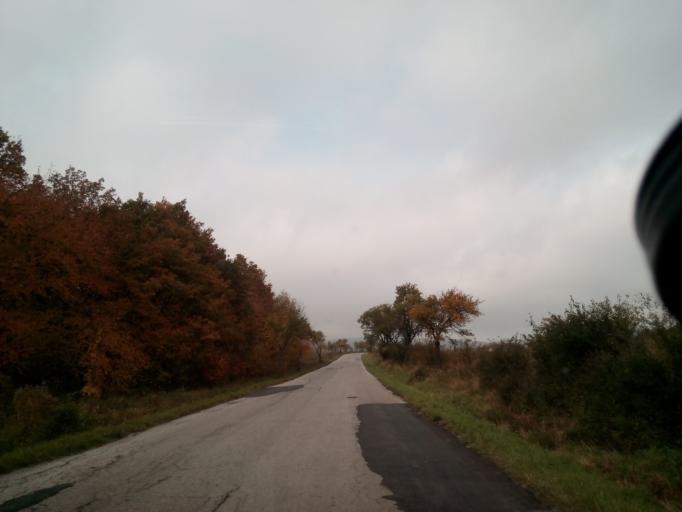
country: SK
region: Kosicky
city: Kosice
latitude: 48.7325
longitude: 21.1313
